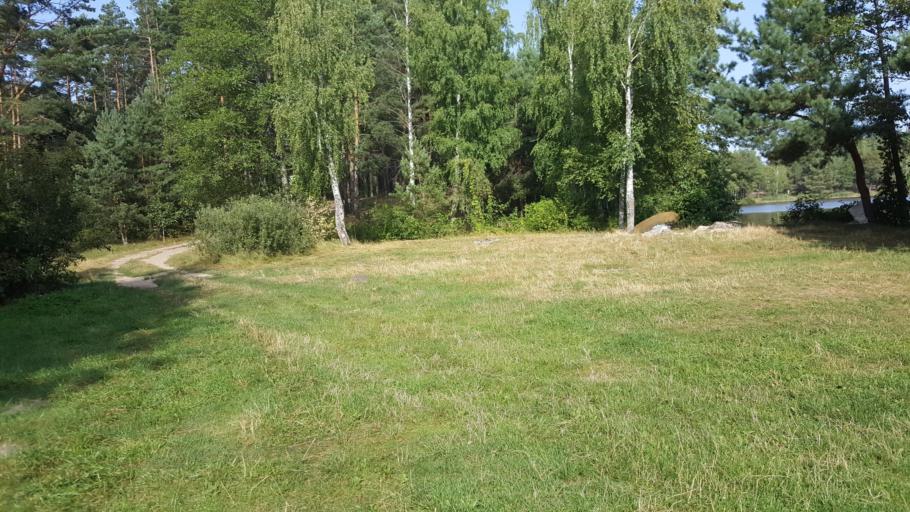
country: BY
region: Brest
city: Ivatsevichy
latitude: 52.7913
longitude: 25.5569
